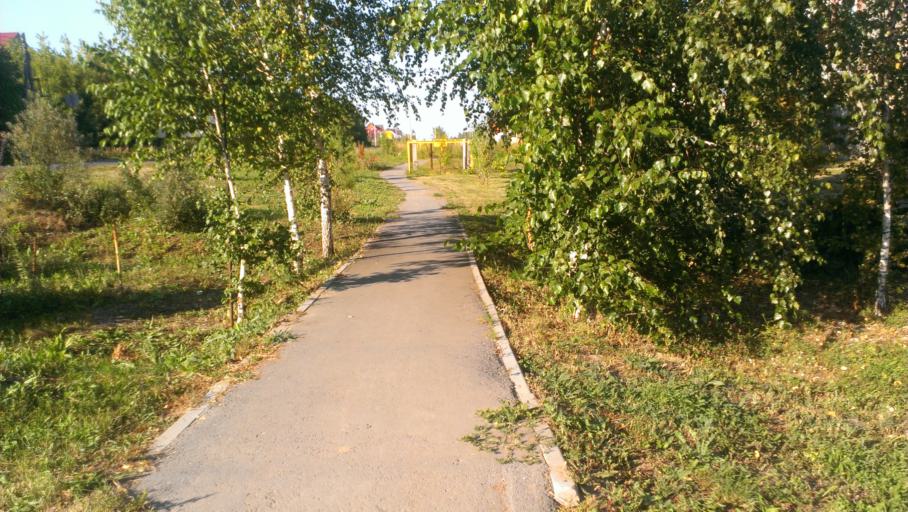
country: RU
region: Altai Krai
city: Novosilikatnyy
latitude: 53.3628
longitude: 83.6436
